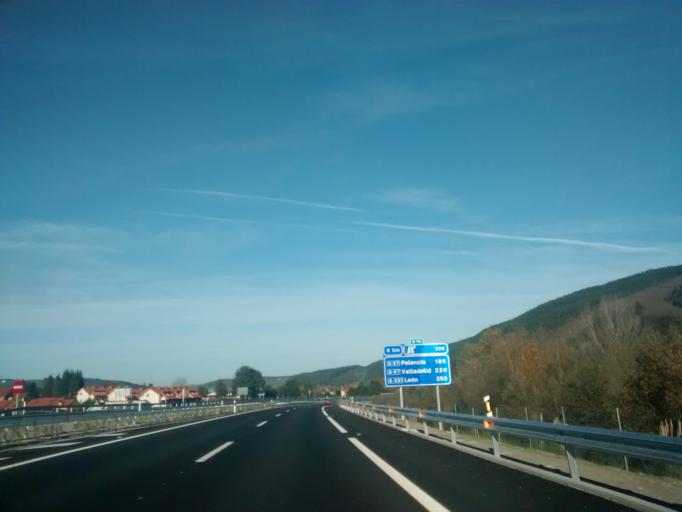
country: ES
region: Cantabria
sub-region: Provincia de Cantabria
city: Puente Viesgo
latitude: 43.3143
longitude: -3.9475
